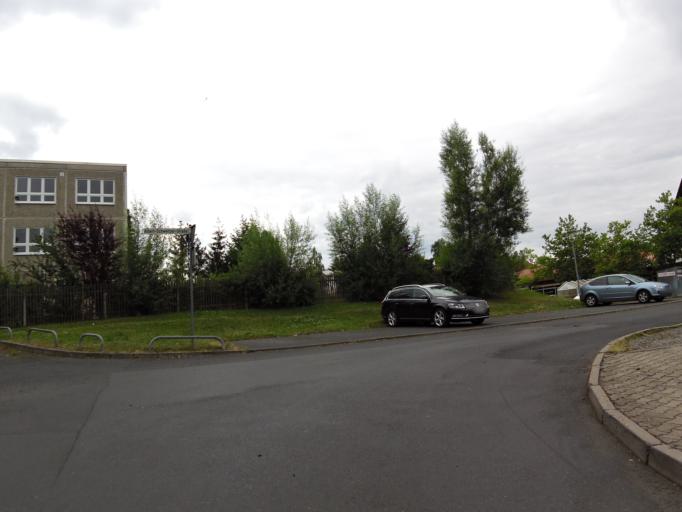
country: DE
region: Thuringia
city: Bad Salzungen
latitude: 50.8067
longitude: 10.2432
